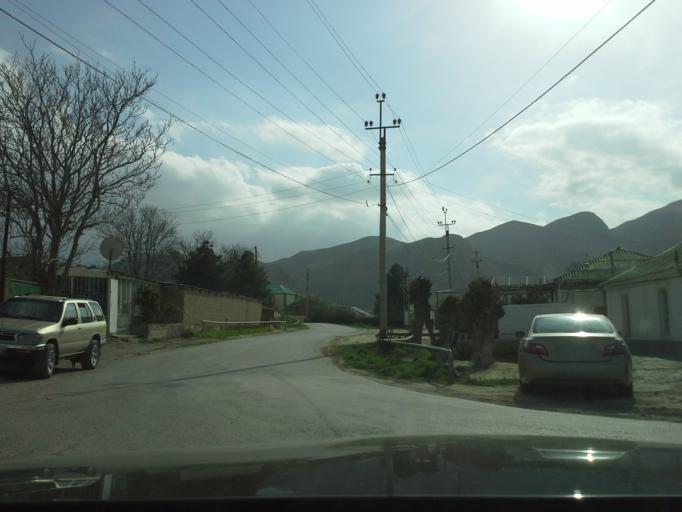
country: TM
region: Ahal
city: Abadan
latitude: 37.9538
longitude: 58.2070
